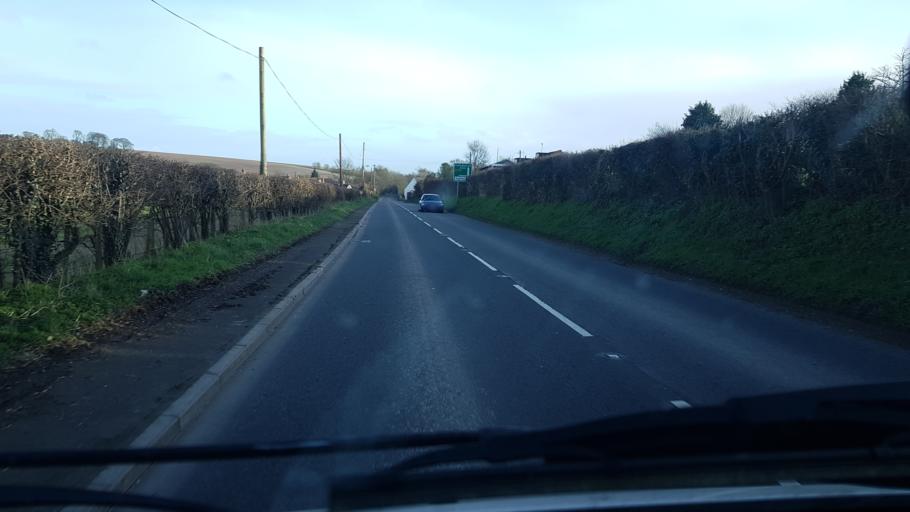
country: GB
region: England
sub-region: Wiltshire
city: Collingbourne Kingston
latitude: 51.3080
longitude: -1.6614
